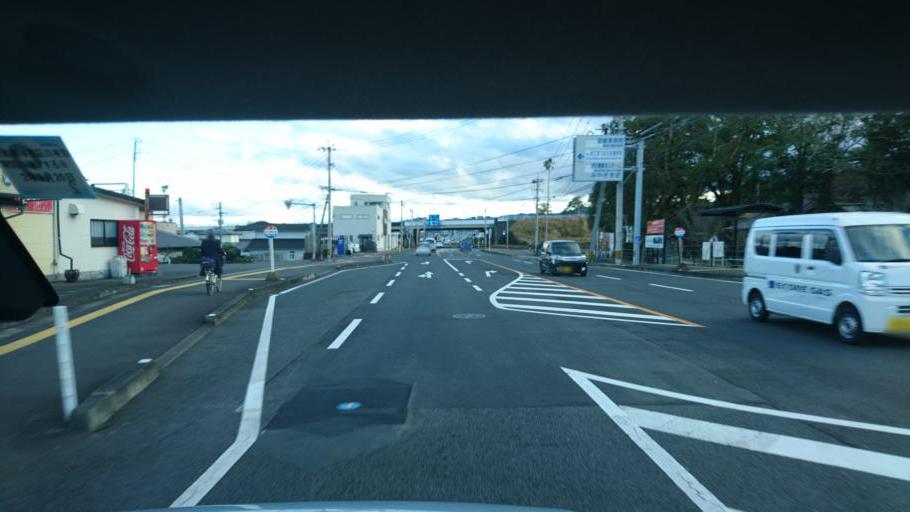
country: JP
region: Miyazaki
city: Miyazaki-shi
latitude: 31.8687
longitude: 131.4317
